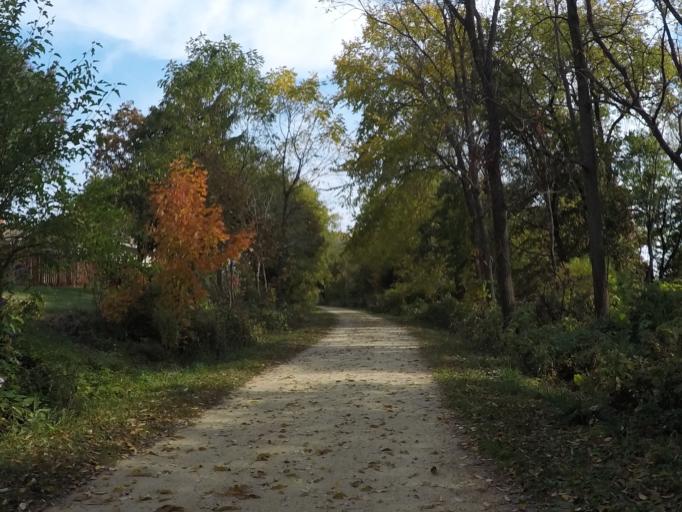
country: US
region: Wisconsin
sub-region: Dane County
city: Mount Horeb
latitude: 43.0081
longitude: -89.7289
